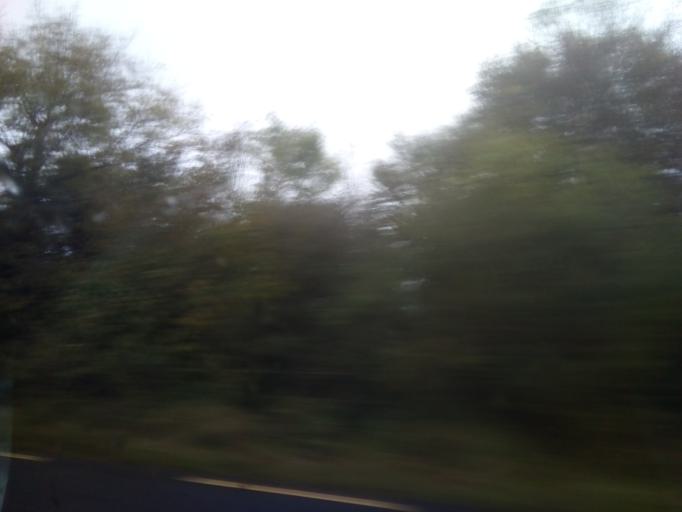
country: IE
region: Connaught
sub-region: Roscommon
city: Castlerea
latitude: 53.8583
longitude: -8.3975
